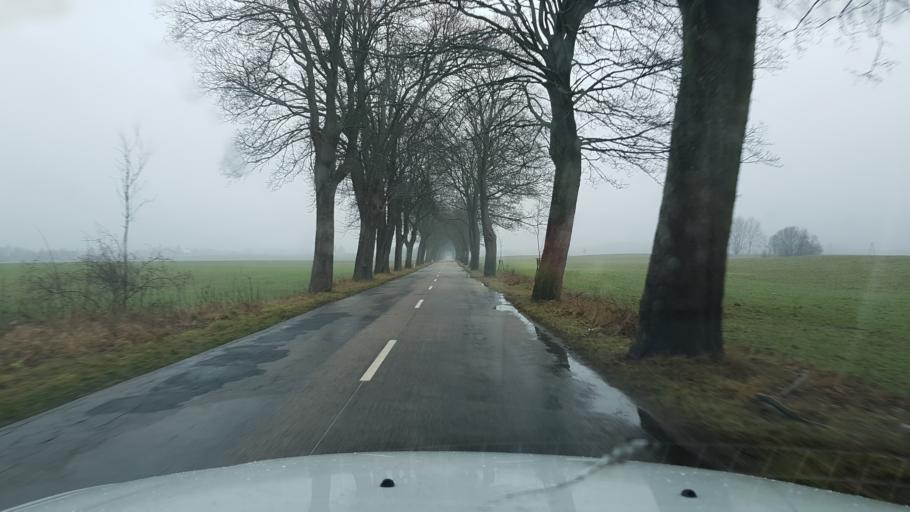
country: PL
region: West Pomeranian Voivodeship
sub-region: Powiat drawski
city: Czaplinek
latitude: 53.5758
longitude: 16.2351
